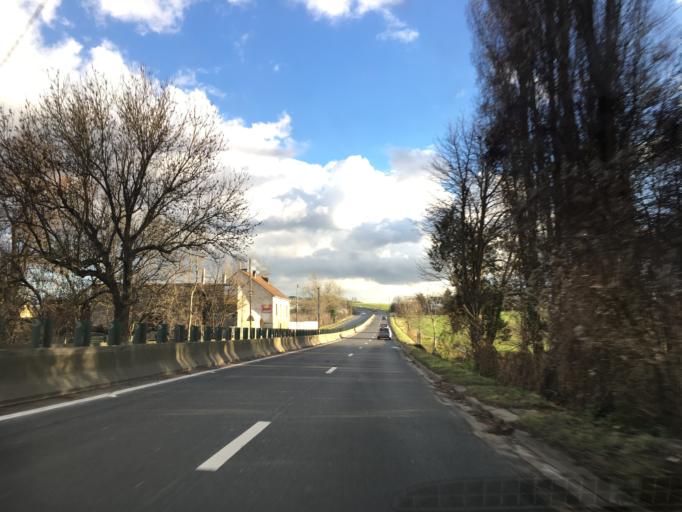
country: FR
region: Ile-de-France
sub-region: Departement du Val-de-Marne
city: Ormesson-sur-Marne
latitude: 48.7885
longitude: 2.5613
